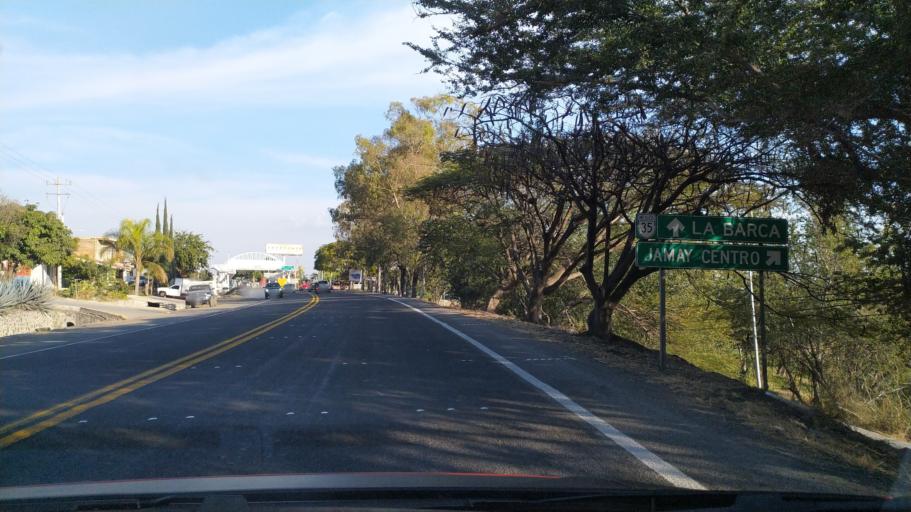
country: MX
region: Jalisco
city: Jamay
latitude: 20.2921
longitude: -102.7231
